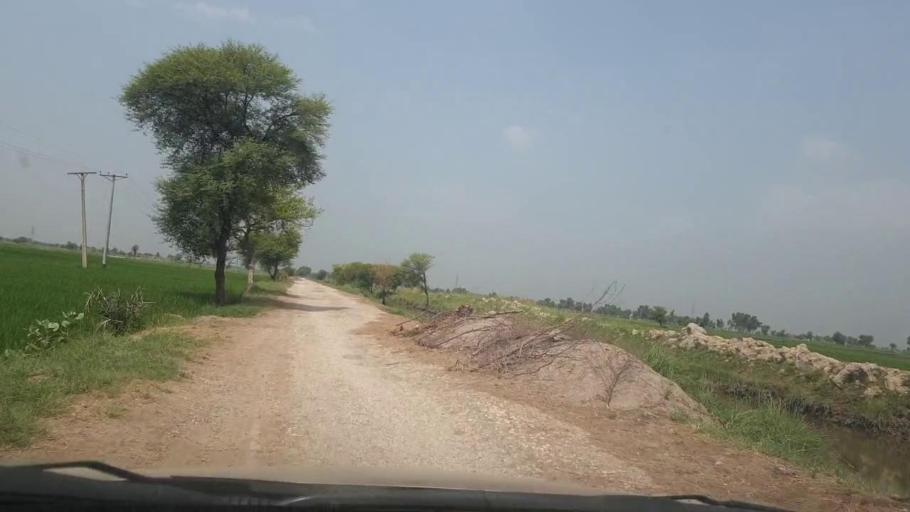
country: PK
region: Sindh
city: Naudero
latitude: 27.6875
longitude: 68.2569
